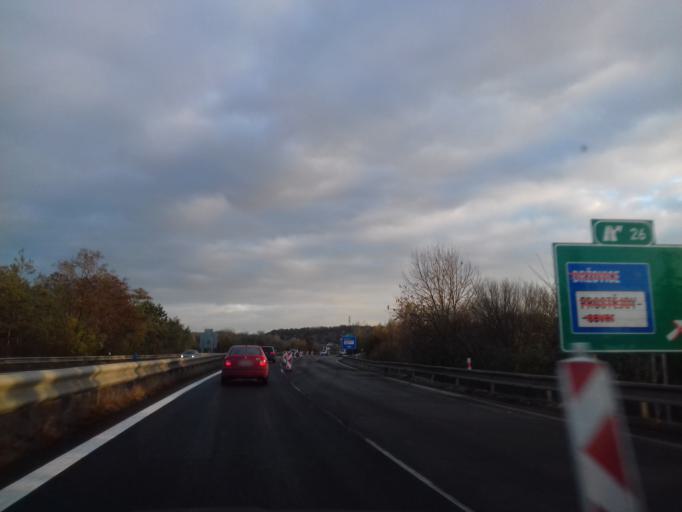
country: CZ
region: Olomoucky
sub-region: Okres Prostejov
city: Prostejov
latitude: 49.4819
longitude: 17.1311
